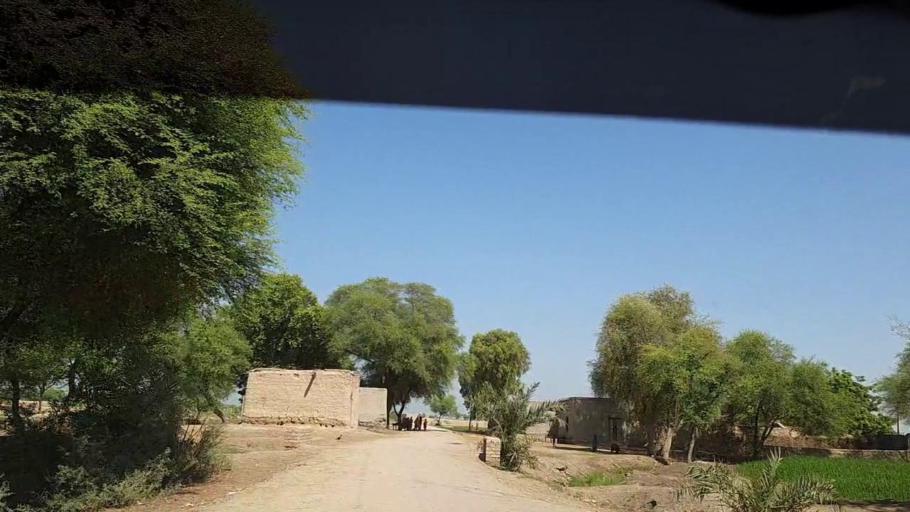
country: PK
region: Sindh
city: Tangwani
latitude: 28.2915
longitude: 69.0852
